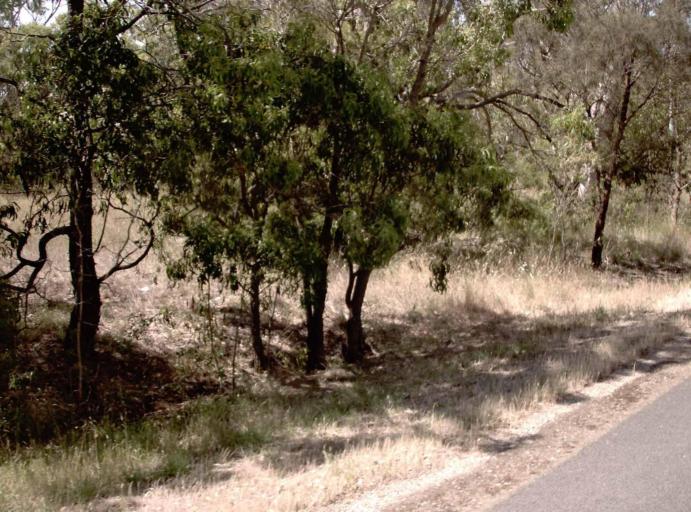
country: AU
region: Victoria
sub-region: Wellington
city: Sale
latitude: -37.9502
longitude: 147.1130
